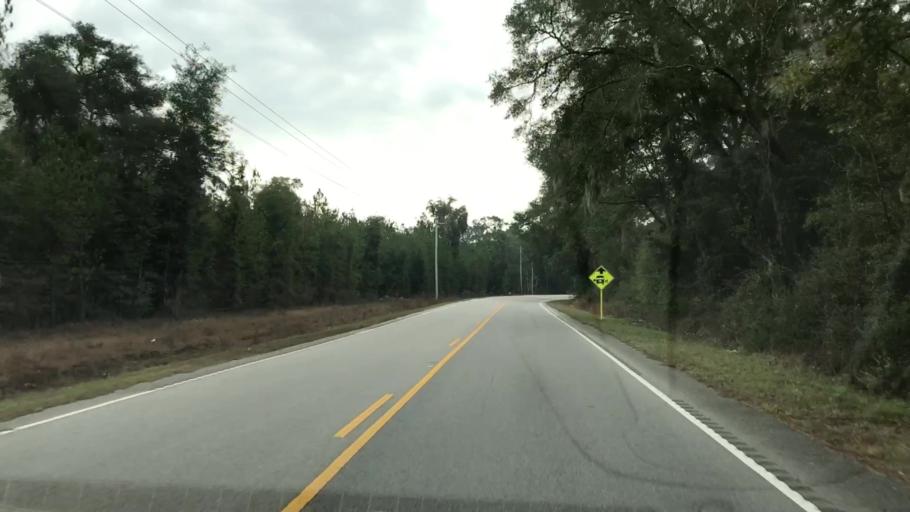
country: US
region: South Carolina
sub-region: Jasper County
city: Ridgeland
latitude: 32.4981
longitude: -80.8853
